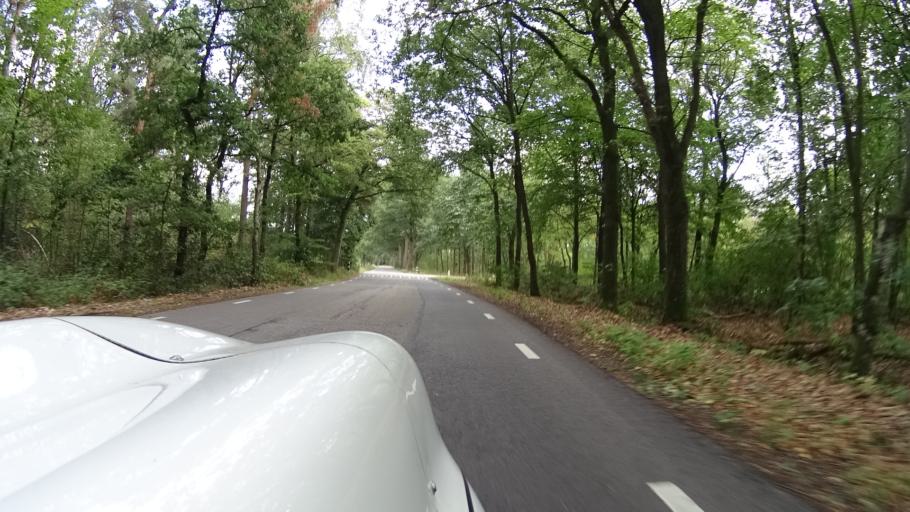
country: NL
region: North Brabant
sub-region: Gemeente Maasdonk
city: Geffen
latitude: 51.6944
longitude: 5.4402
